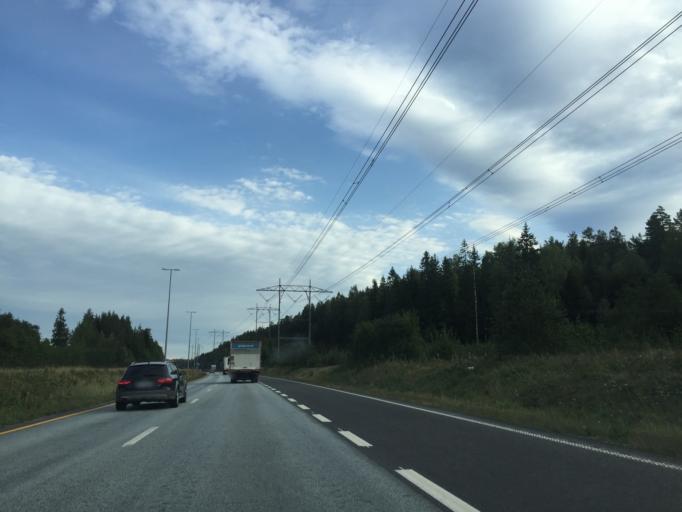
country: NO
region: Akershus
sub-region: Oppegard
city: Kolbotn
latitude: 59.7991
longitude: 10.8432
